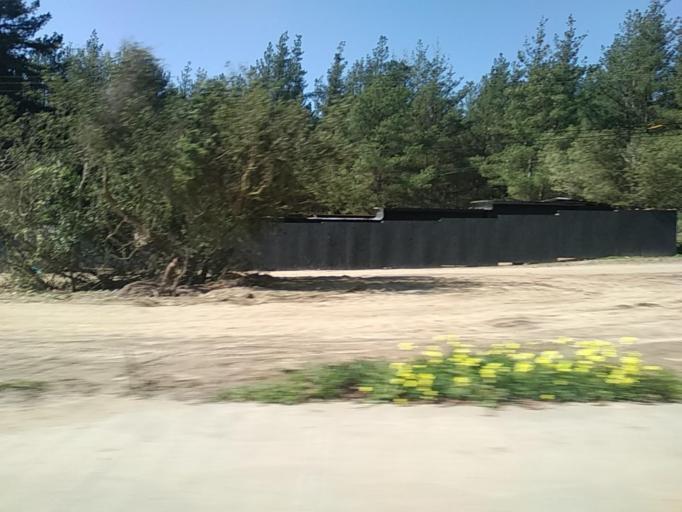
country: CL
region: Valparaiso
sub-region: Provincia de Valparaiso
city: Vina del Mar
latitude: -32.9551
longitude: -71.5390
